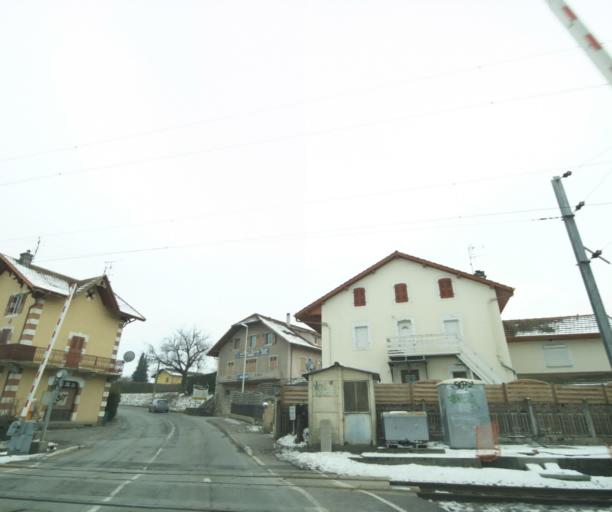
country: FR
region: Rhone-Alpes
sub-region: Departement de la Haute-Savoie
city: Reignier-Esery
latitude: 46.1262
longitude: 6.2661
